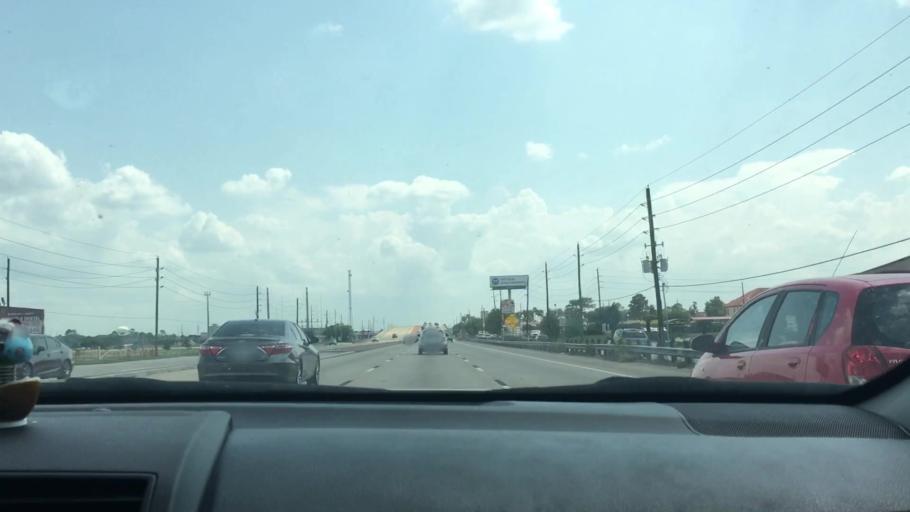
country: US
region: Texas
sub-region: Fort Bend County
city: Mission Bend
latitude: 29.7163
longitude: -95.6445
